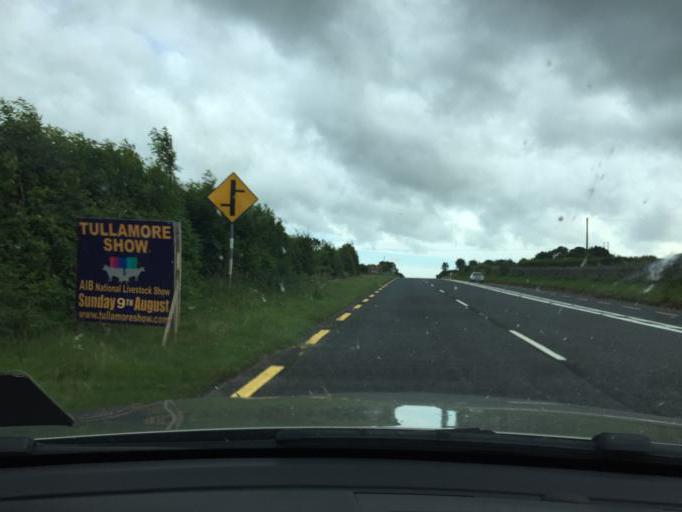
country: IE
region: Munster
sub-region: Waterford
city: Dungarvan
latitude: 52.1289
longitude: -7.5633
